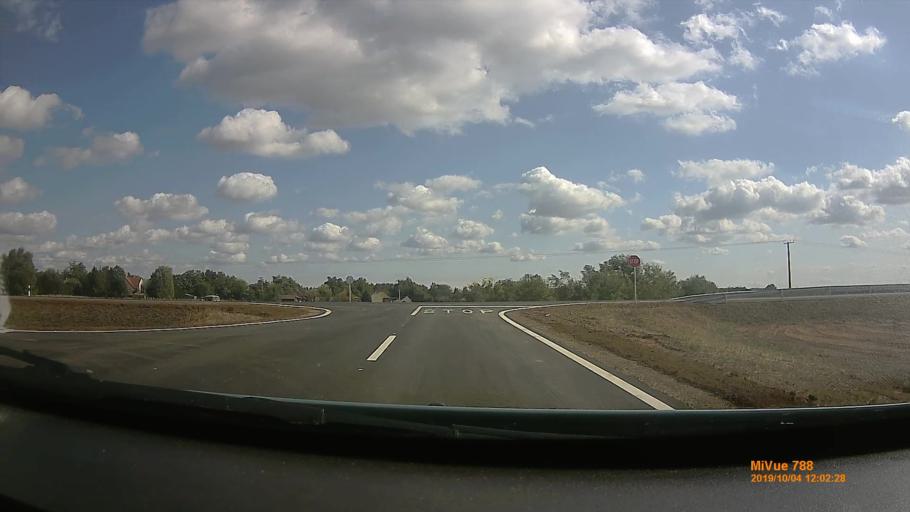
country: HU
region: Szabolcs-Szatmar-Bereg
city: Nyirtelek
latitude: 48.0196
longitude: 21.6789
